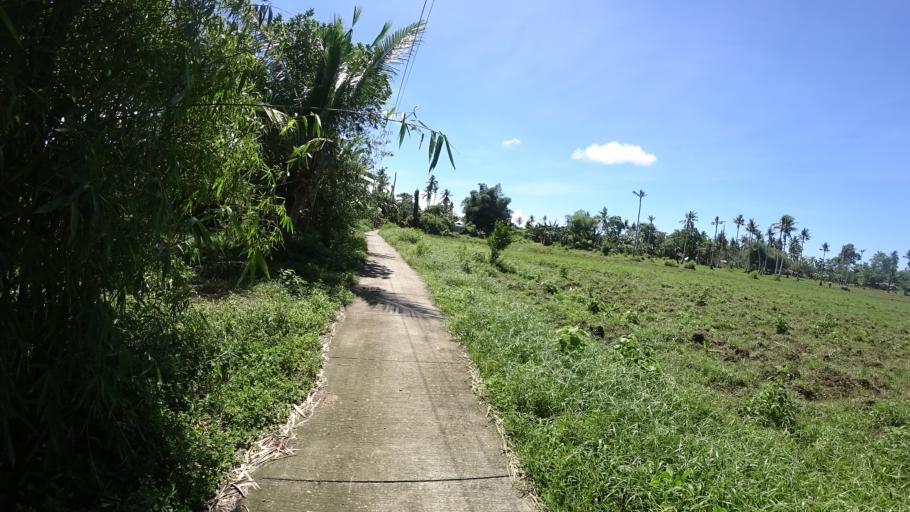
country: PH
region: Eastern Visayas
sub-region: Province of Leyte
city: Cabacungan
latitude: 10.9191
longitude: 124.9796
